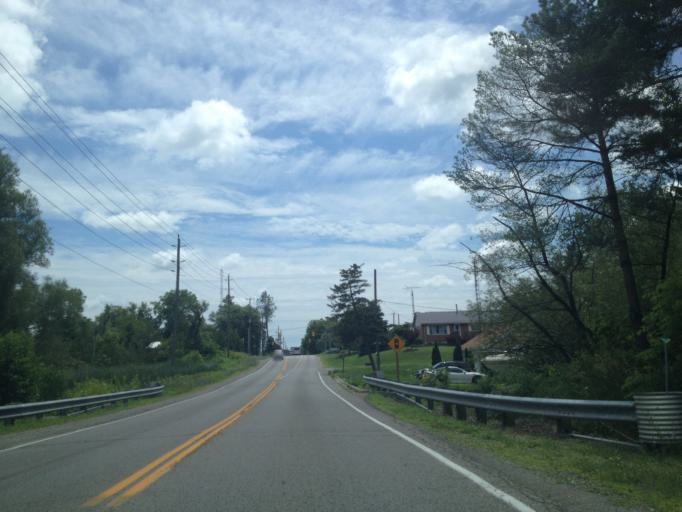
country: CA
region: Ontario
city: Norfolk County
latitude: 42.8311
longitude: -80.3371
